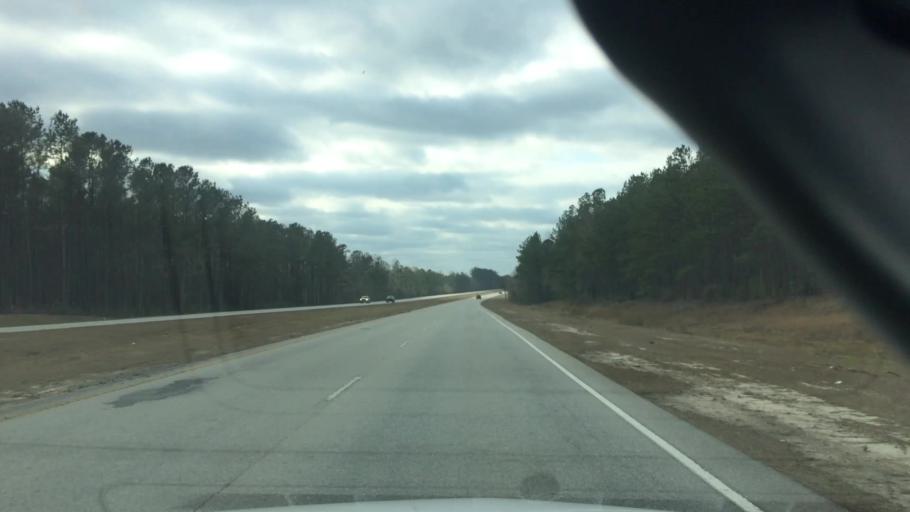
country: US
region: North Carolina
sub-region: Brunswick County
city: Bolivia
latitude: 34.0685
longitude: -78.1779
